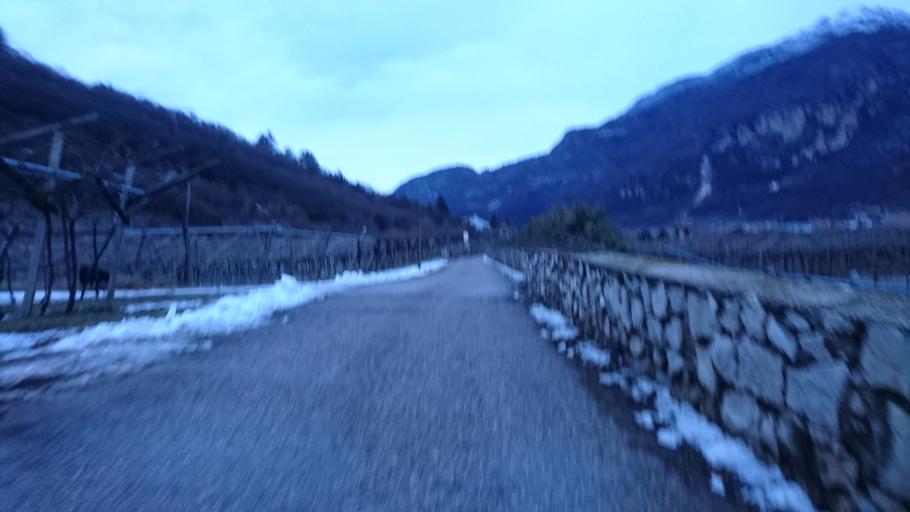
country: IT
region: Trentino-Alto Adige
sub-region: Provincia di Trento
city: Mori
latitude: 45.8418
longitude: 10.9898
